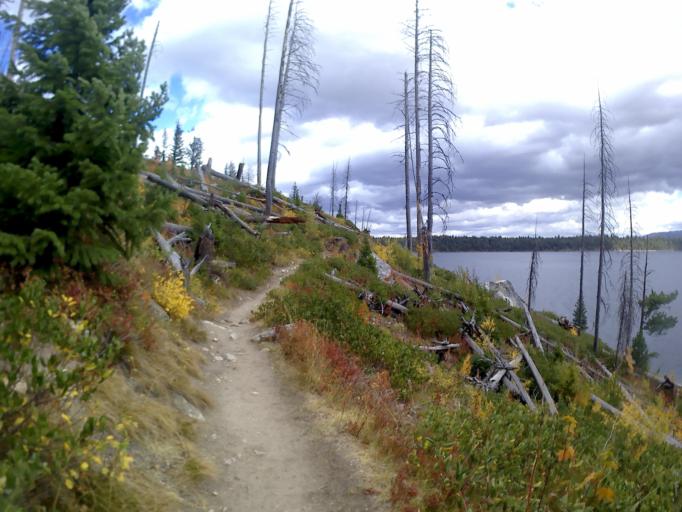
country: US
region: Wyoming
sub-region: Teton County
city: Moose Wilson Road
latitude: 43.7733
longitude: -110.7388
